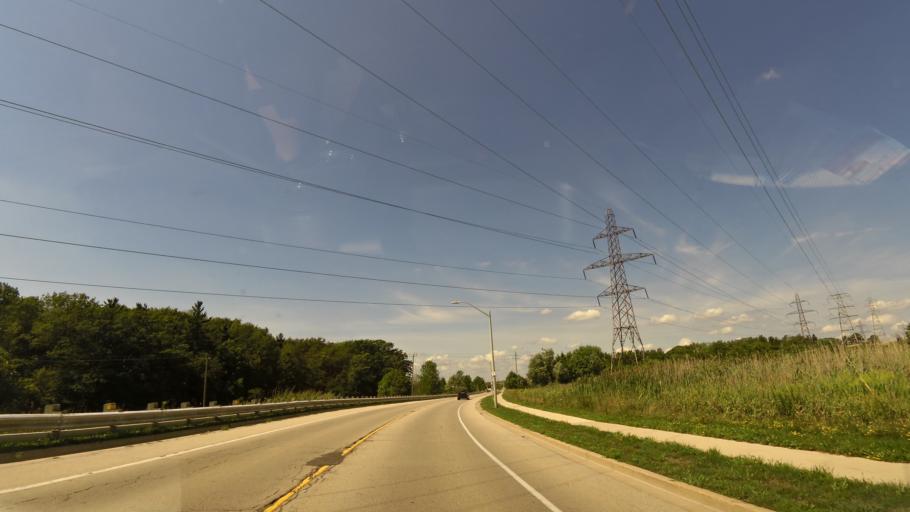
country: CA
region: Ontario
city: Ancaster
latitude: 43.2206
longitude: -79.9293
